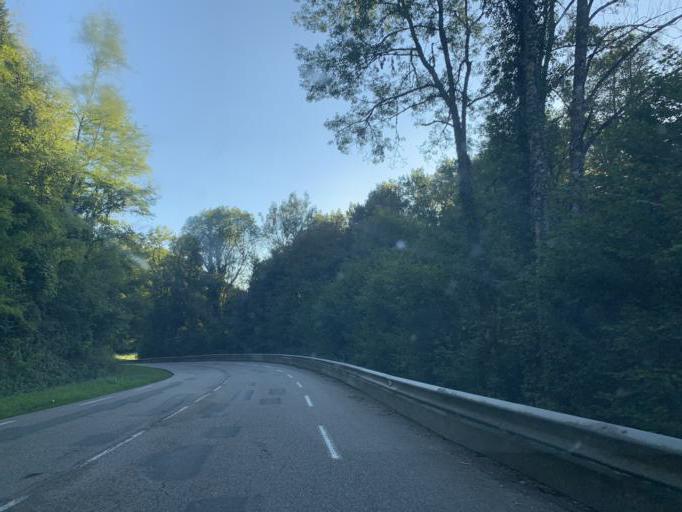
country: FR
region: Rhone-Alpes
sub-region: Departement de l'Ain
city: Belley
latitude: 45.7330
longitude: 5.6689
